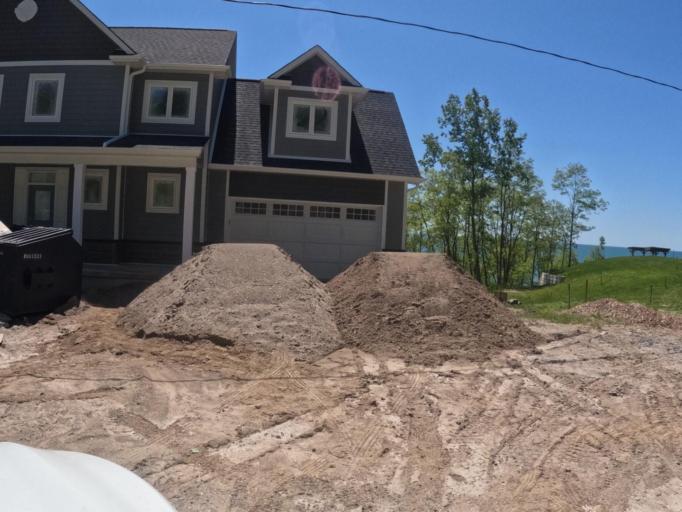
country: CA
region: Ontario
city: Norfolk County
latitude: 42.7780
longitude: -80.2313
